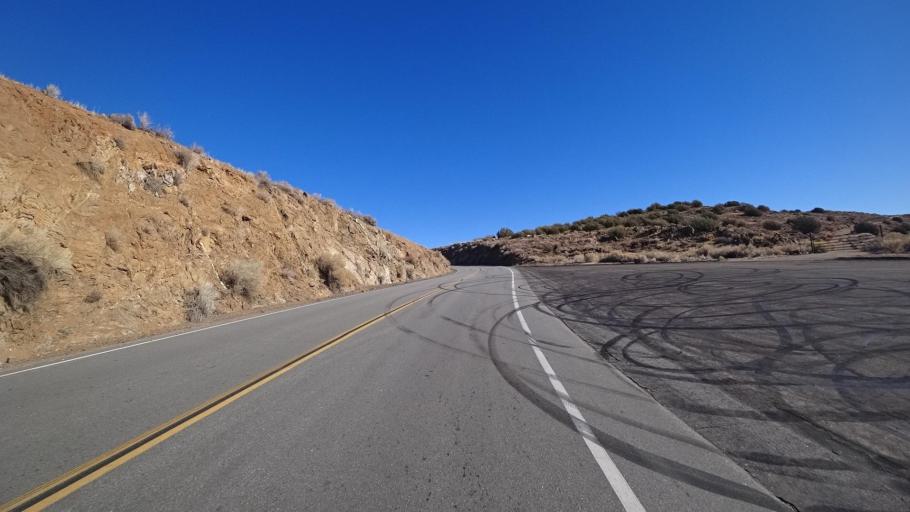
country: US
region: California
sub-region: Kern County
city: Wofford Heights
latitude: 35.6822
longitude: -118.3893
